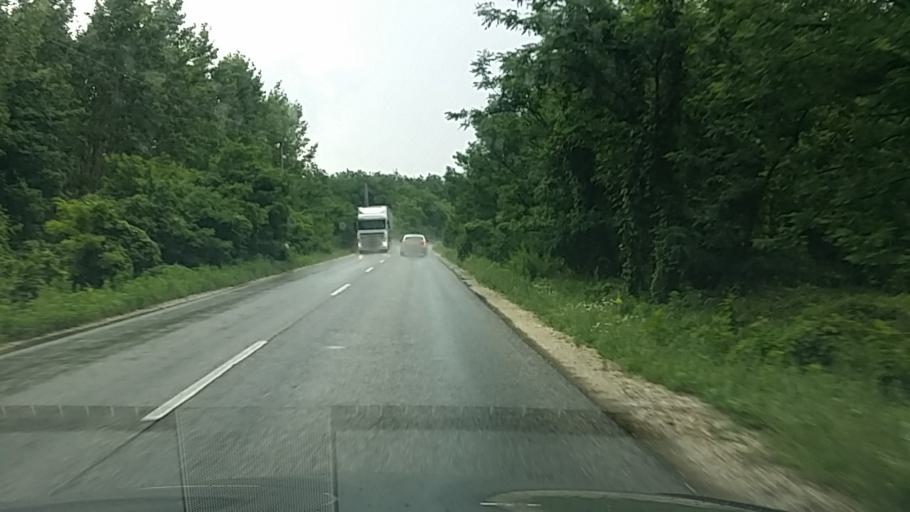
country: HU
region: Pest
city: Inarcs
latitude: 47.3310
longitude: 19.3091
